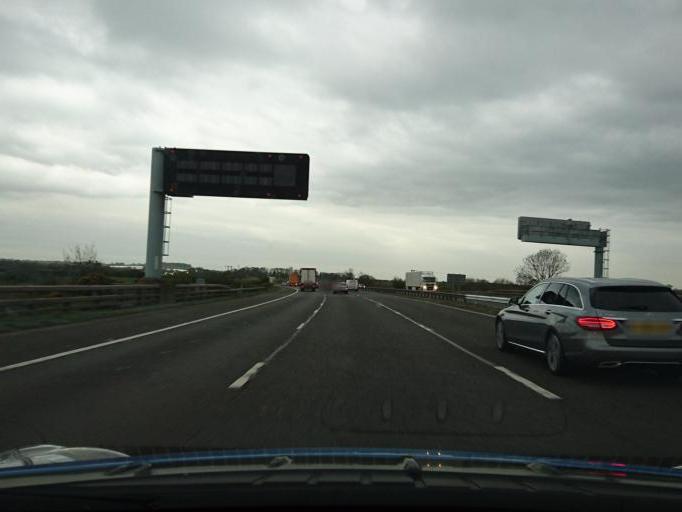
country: GB
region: England
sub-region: Staffordshire
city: Stafford
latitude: 52.8202
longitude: -2.1529
